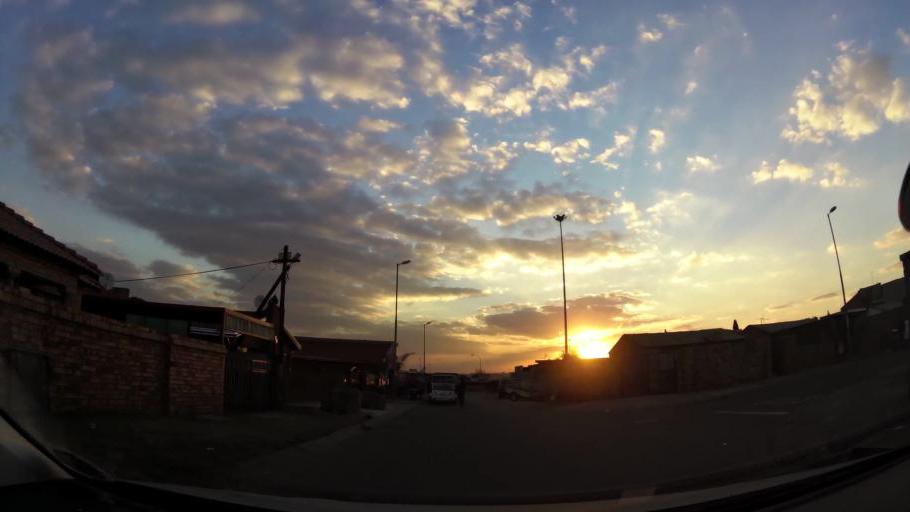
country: ZA
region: Gauteng
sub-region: City of Johannesburg Metropolitan Municipality
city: Soweto
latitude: -26.2755
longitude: 27.8997
